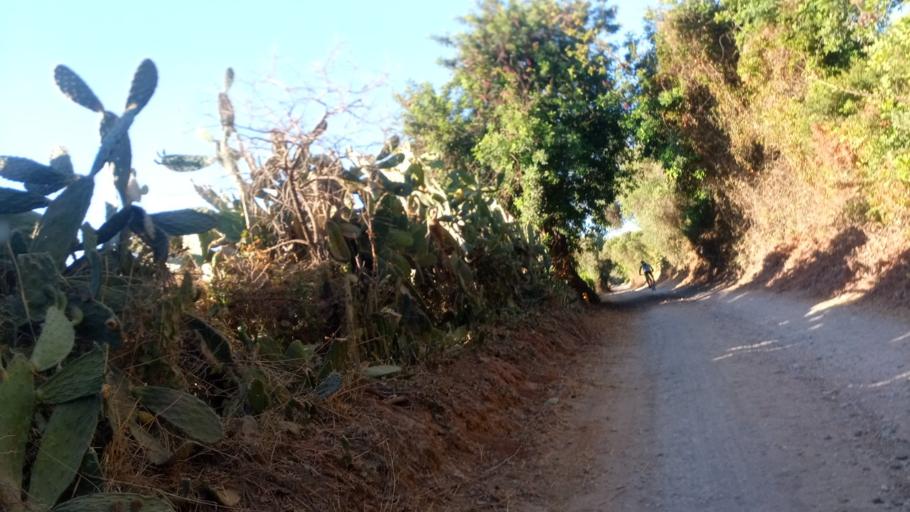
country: PT
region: Faro
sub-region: Tavira
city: Tavira
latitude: 37.1458
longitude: -7.5934
